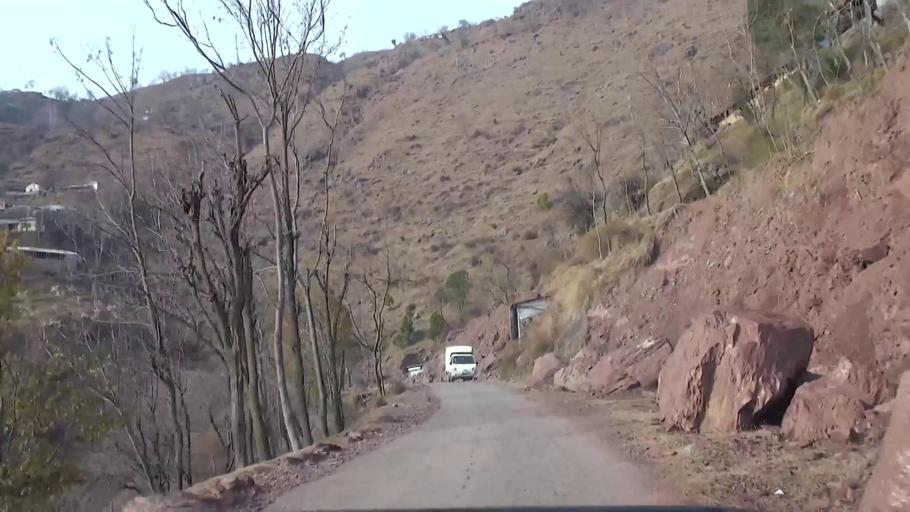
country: PK
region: Azad Kashmir
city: Muzaffarabad
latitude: 34.3691
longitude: 73.5245
